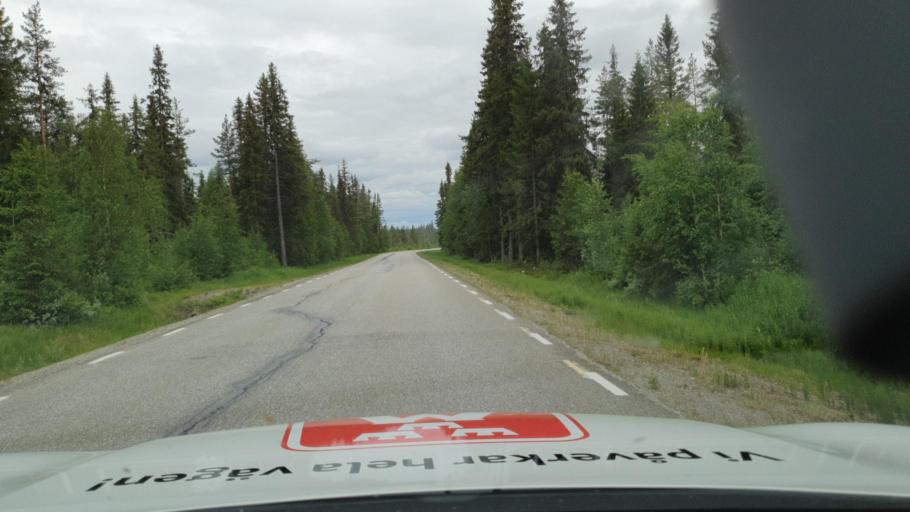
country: SE
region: Vaesterbotten
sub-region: Lycksele Kommun
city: Soderfors
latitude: 64.3089
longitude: 18.1674
